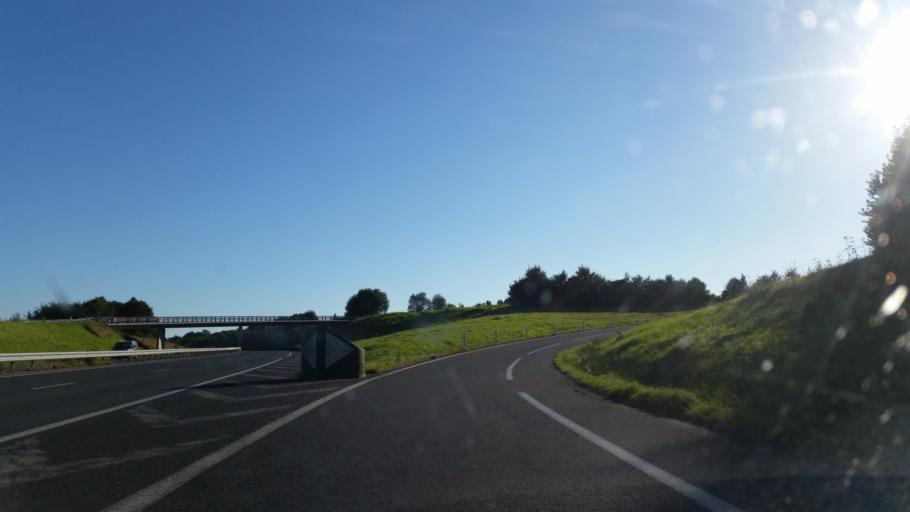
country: FR
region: Lower Normandy
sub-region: Departement du Calvados
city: La Riviere-Saint-Sauveur
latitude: 49.3900
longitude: 0.2552
